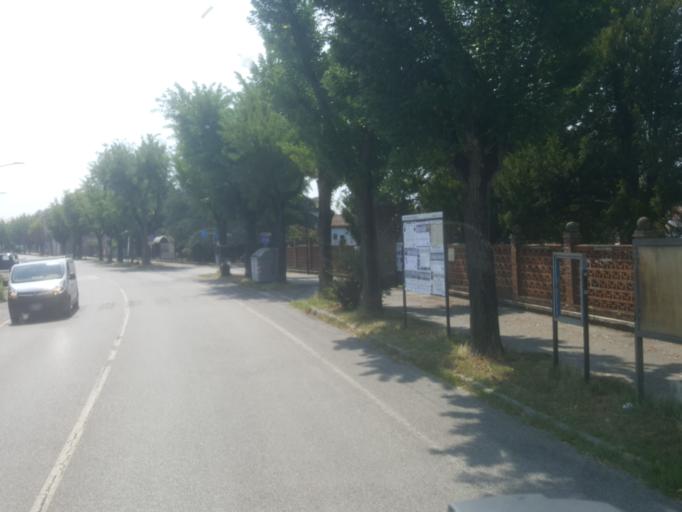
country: IT
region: Emilia-Romagna
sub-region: Provincia di Ravenna
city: Lavezzola
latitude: 44.5649
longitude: 11.8729
